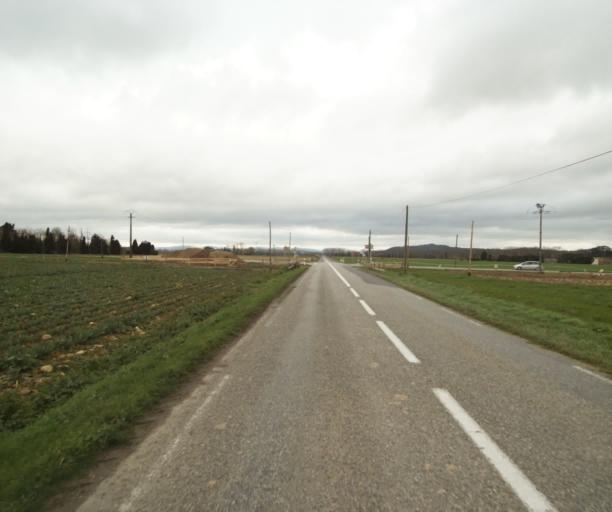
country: FR
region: Midi-Pyrenees
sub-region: Departement de l'Ariege
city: Saverdun
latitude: 43.2055
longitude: 1.6252
